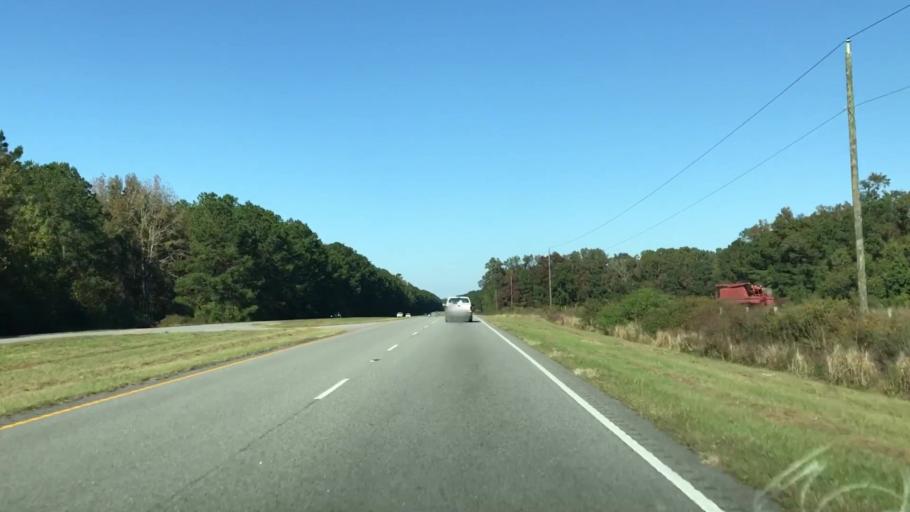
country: US
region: South Carolina
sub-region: Hampton County
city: Yemassee
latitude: 32.6133
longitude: -80.8137
